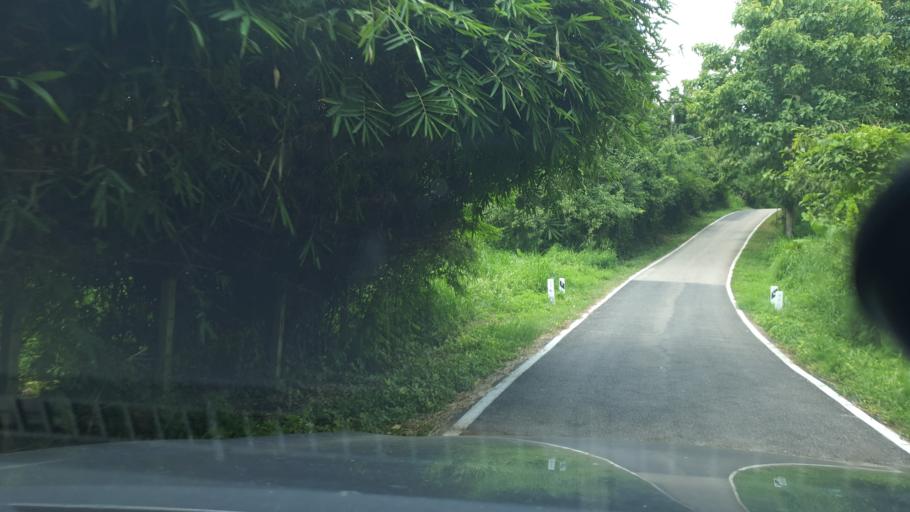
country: TH
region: Lampang
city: Hang Chat
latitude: 18.4100
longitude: 99.2626
